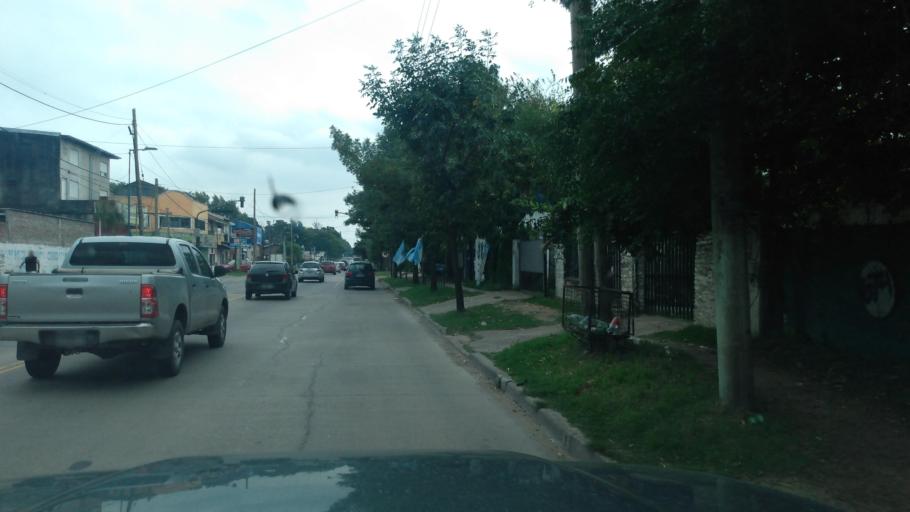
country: AR
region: Buenos Aires
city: Hurlingham
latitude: -34.5768
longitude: -58.6871
